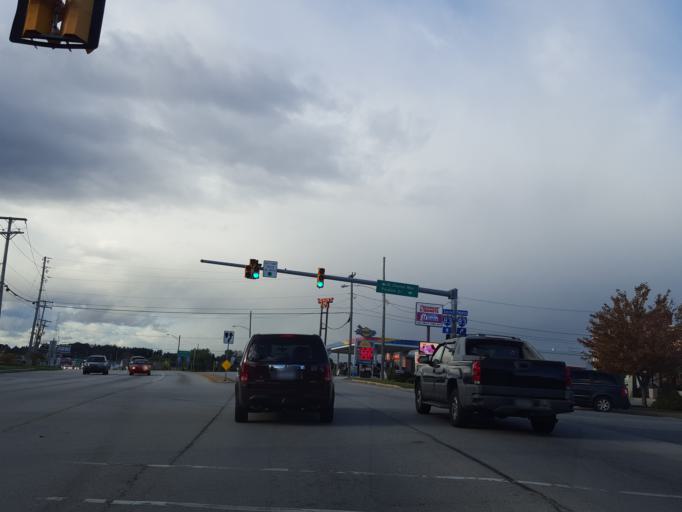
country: US
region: Pennsylvania
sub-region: York County
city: Spry
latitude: 39.9304
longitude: -76.6874
